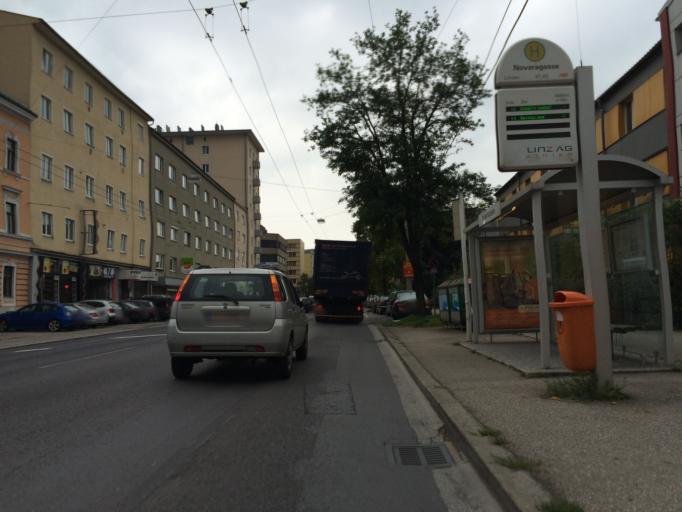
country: AT
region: Upper Austria
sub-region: Linz Stadt
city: Linz
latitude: 48.2874
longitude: 14.2950
